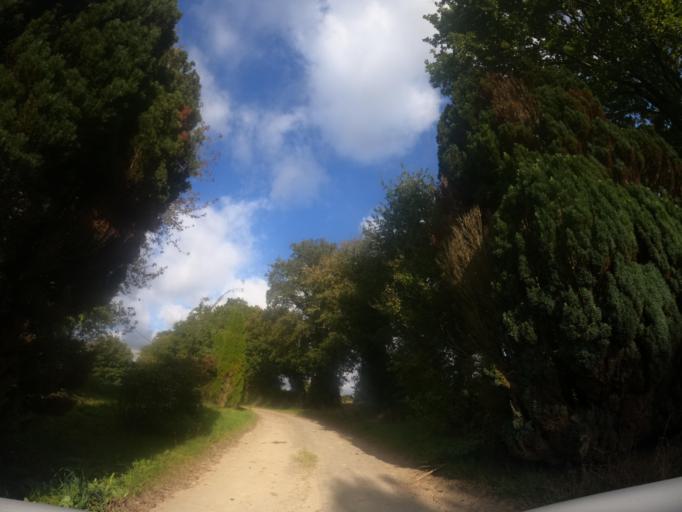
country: FR
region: Poitou-Charentes
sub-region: Departement des Deux-Sevres
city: Courlay
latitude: 46.7852
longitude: -0.6036
